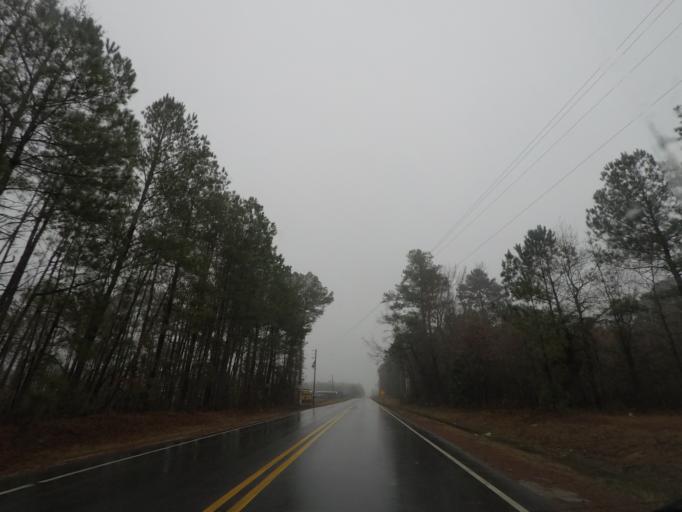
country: US
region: North Carolina
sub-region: Scotland County
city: Laurinburg
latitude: 34.8231
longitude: -79.4586
